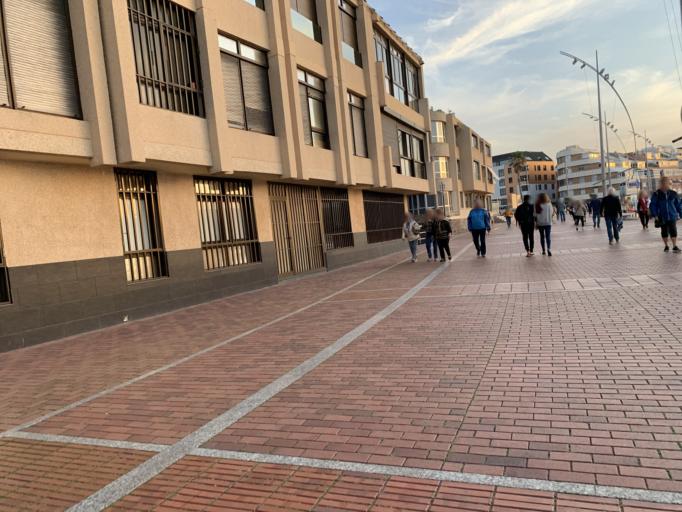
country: ES
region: Canary Islands
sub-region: Provincia de Las Palmas
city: Las Palmas de Gran Canaria
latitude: 28.1354
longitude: -15.4405
